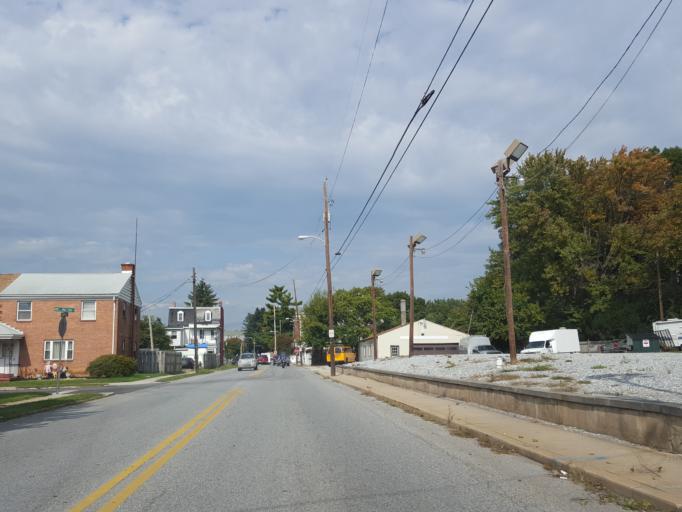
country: US
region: Pennsylvania
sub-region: York County
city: East York
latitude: 39.9698
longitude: -76.7015
